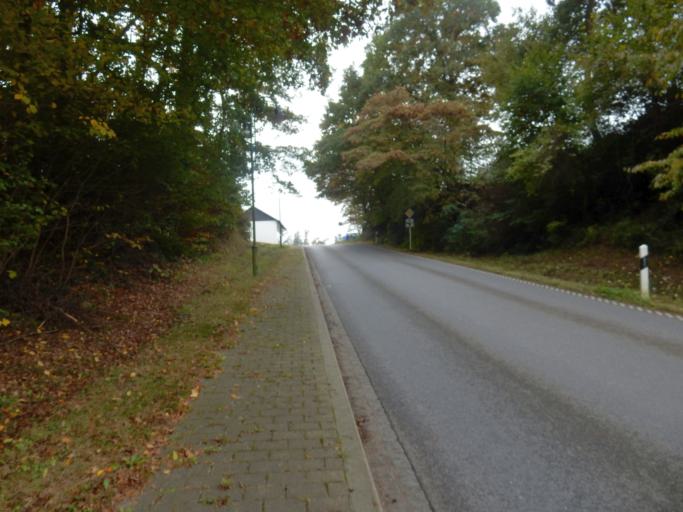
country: LU
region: Luxembourg
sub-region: Canton de Mersch
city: Boevange-sur-Attert
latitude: 49.7518
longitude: 6.0360
